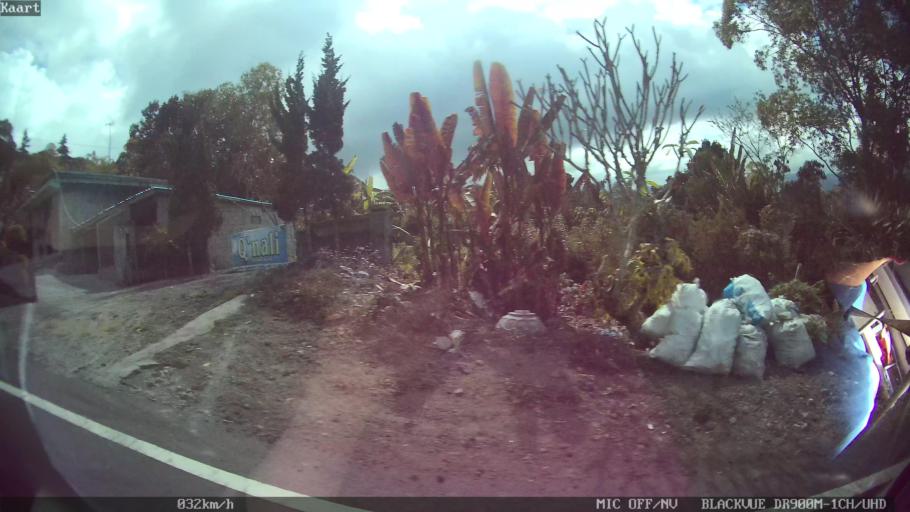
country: ID
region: Bali
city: Banjar Kedisan
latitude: -8.2789
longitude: 115.3703
